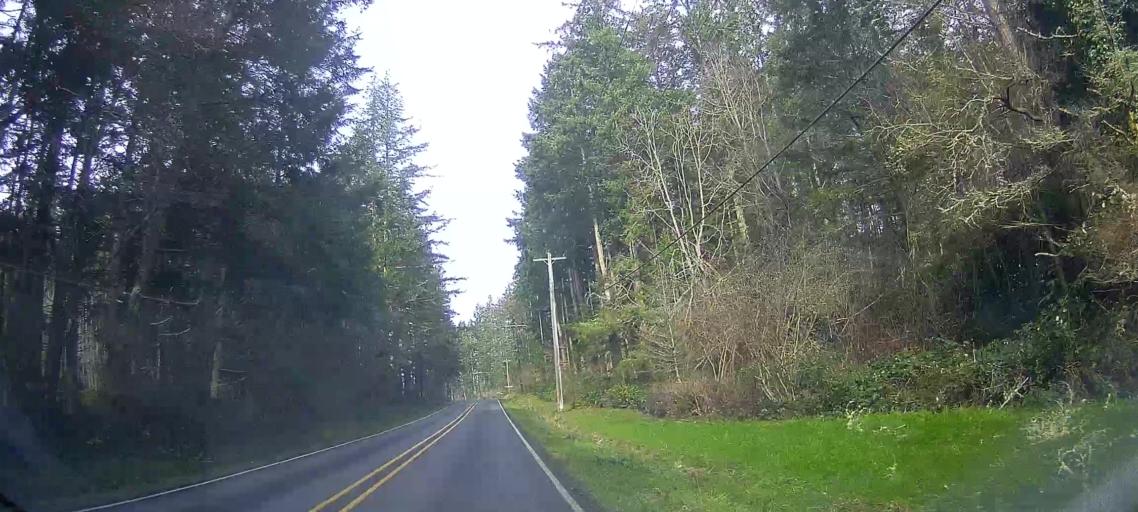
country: US
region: Washington
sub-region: Island County
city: Camano
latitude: 48.2038
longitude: -122.5325
